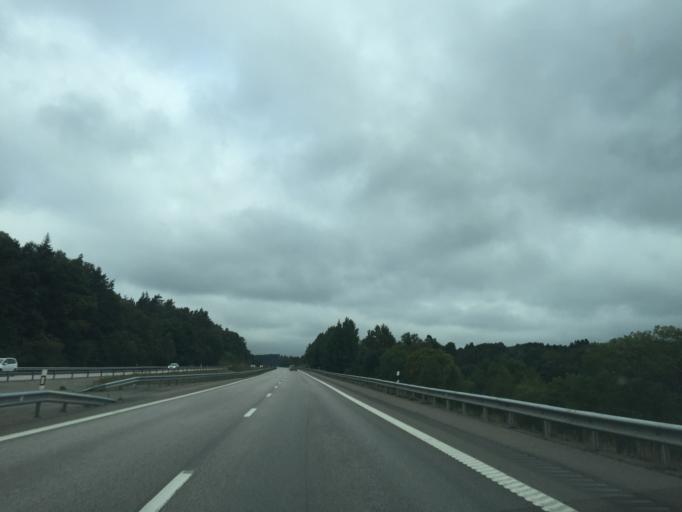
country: SE
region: Halland
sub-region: Kungsbacka Kommun
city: Frillesas
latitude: 57.3726
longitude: 12.2013
